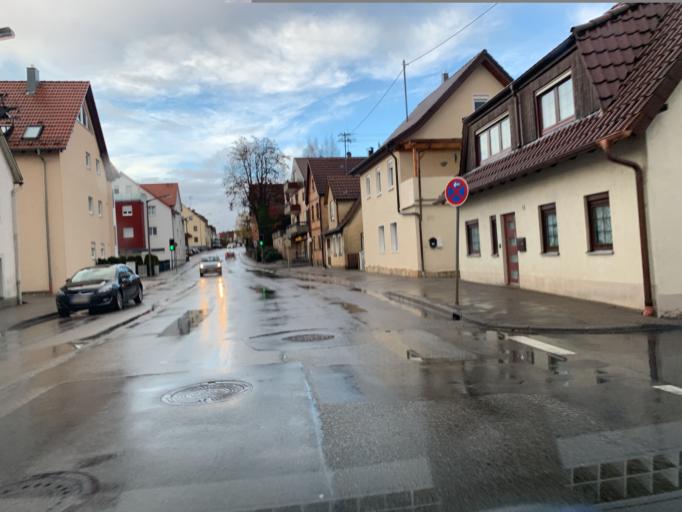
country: DE
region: Baden-Wuerttemberg
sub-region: Regierungsbezirk Stuttgart
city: Magstadt
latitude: 48.7437
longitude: 8.9634
